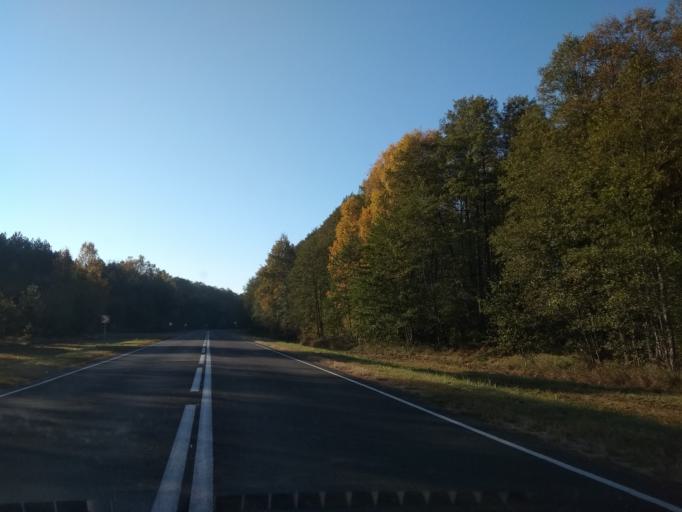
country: BY
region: Brest
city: Kobryn
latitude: 52.0680
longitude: 24.2839
